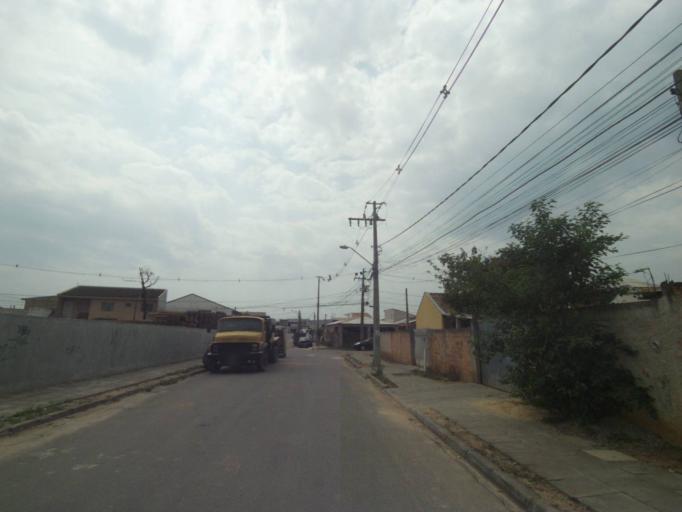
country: BR
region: Parana
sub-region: Sao Jose Dos Pinhais
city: Sao Jose dos Pinhais
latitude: -25.4943
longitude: -49.2029
